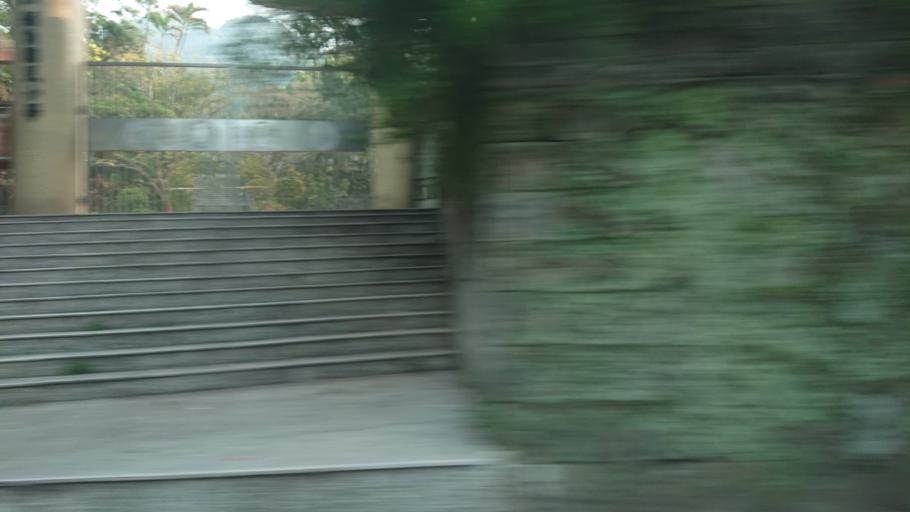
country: TW
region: Taiwan
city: Daxi
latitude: 24.8720
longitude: 121.4051
